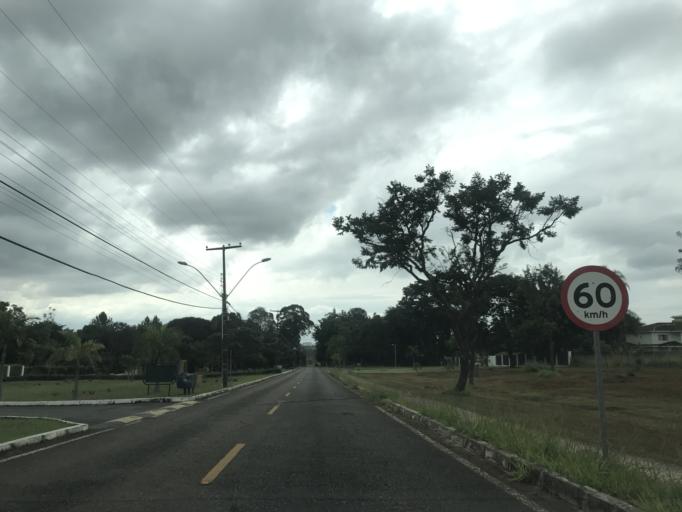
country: BR
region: Federal District
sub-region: Brasilia
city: Brasilia
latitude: -15.8971
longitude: -47.9319
